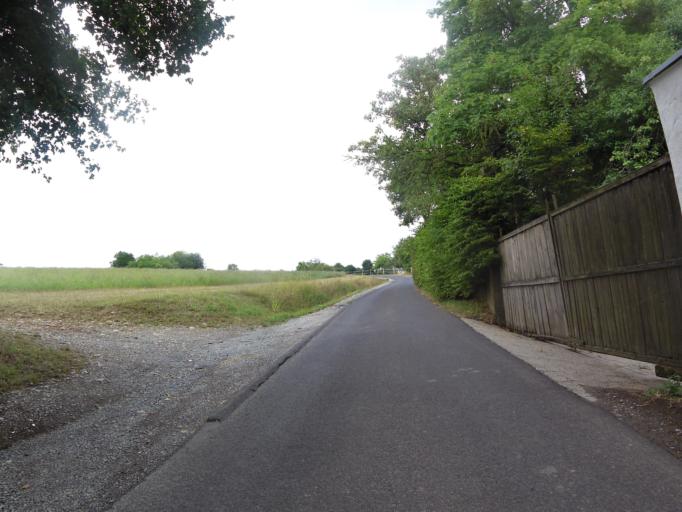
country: DE
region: Bavaria
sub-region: Regierungsbezirk Unterfranken
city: Wuerzburg
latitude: 49.7682
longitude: 9.8759
